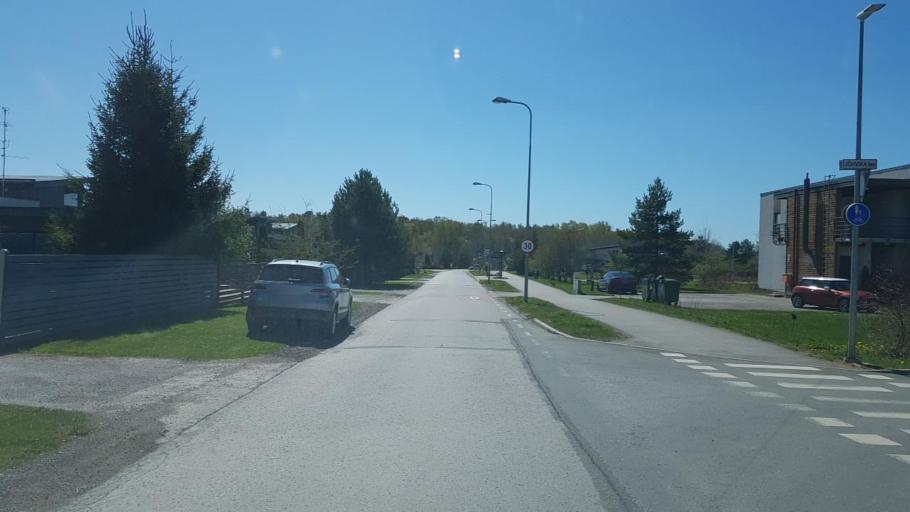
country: EE
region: Harju
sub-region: Viimsi vald
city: Viimsi
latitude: 59.5017
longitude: 24.8585
